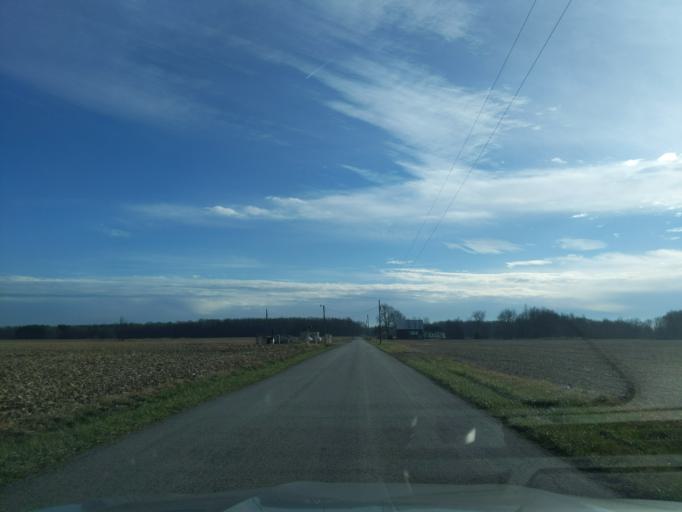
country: US
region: Indiana
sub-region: Decatur County
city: Westport
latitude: 39.1951
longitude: -85.4618
